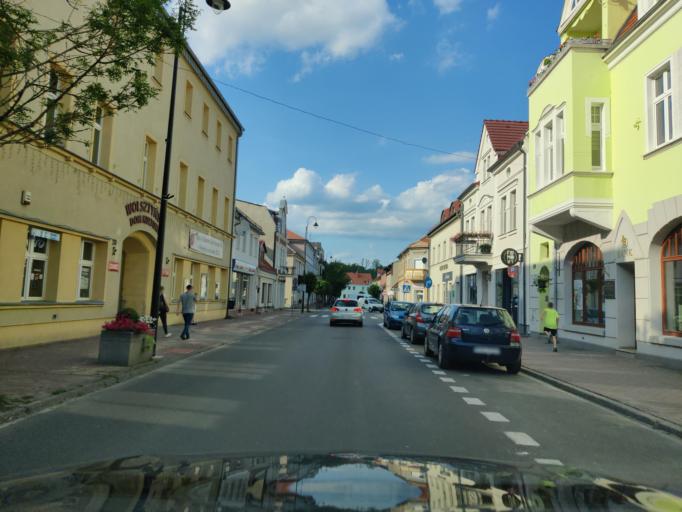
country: PL
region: Greater Poland Voivodeship
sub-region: Powiat wolsztynski
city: Wolsztyn
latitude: 52.1160
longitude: 16.1099
